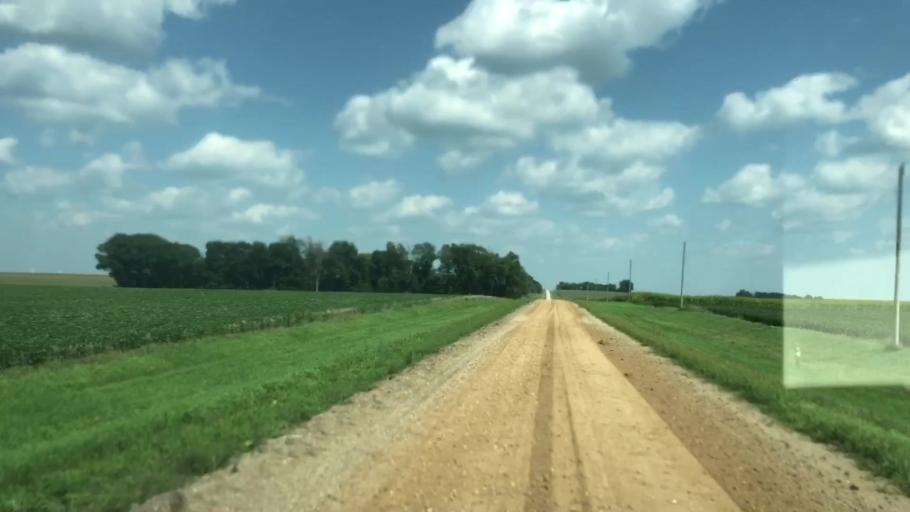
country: US
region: Iowa
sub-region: O'Brien County
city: Sheldon
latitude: 43.1568
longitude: -95.7903
